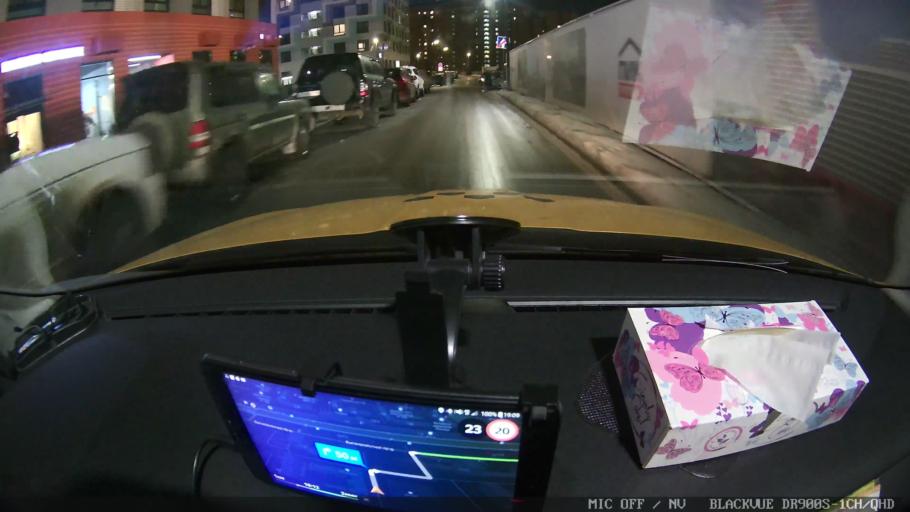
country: RU
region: Moscow
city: Bibirevo
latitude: 55.8756
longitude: 37.6019
